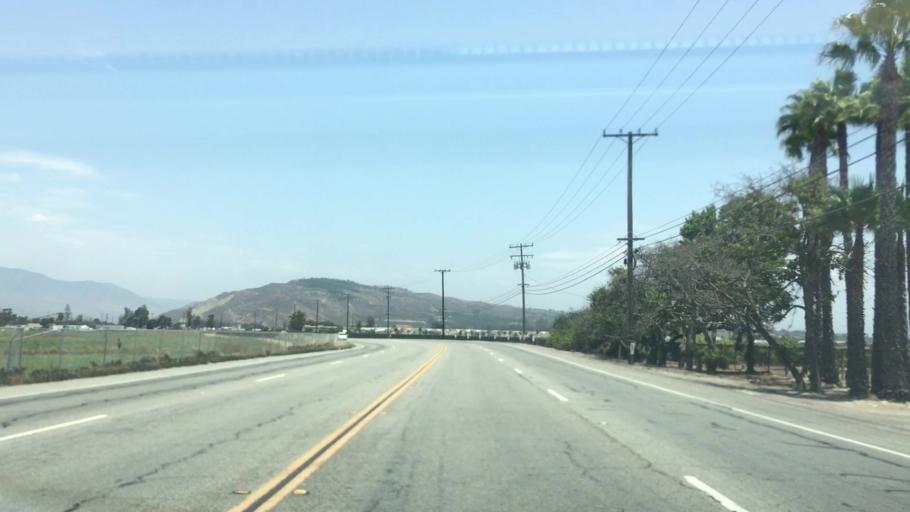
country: US
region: California
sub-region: Ventura County
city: Saticoy
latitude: 34.2618
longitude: -119.1489
